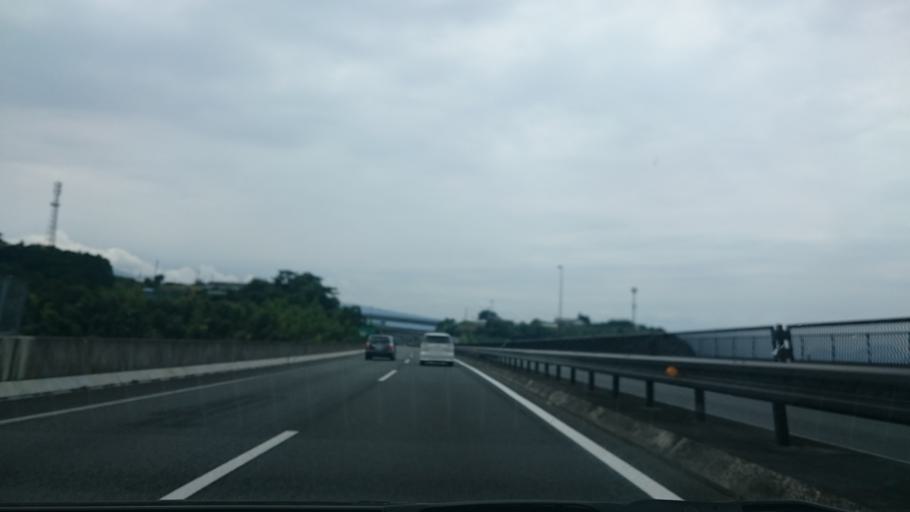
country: JP
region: Shizuoka
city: Mishima
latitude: 35.1358
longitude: 138.9397
